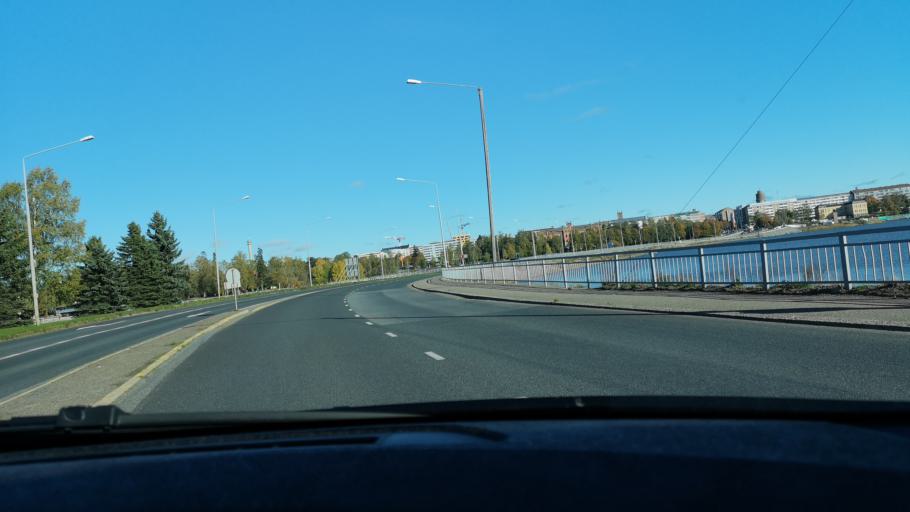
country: FI
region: Ostrobothnia
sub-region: Vaasa
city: Vaasa
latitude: 63.0915
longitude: 21.5904
